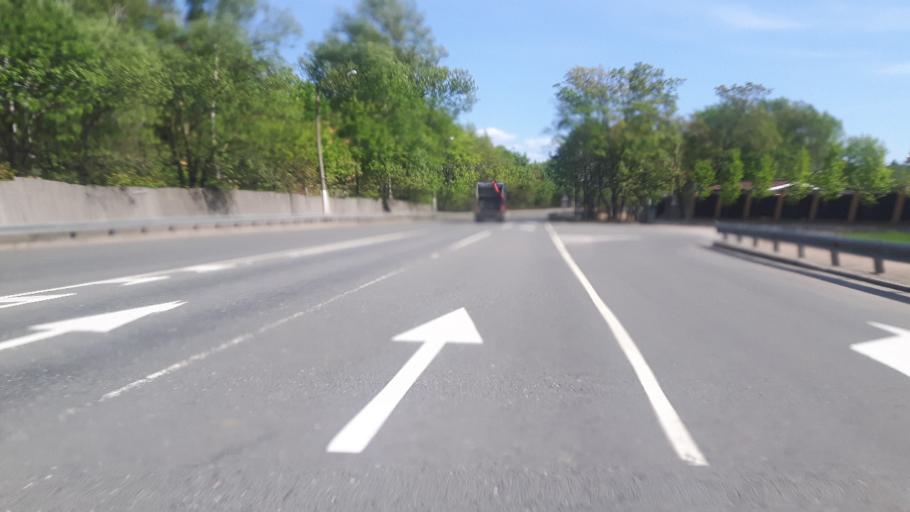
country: RU
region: Leningrad
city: Vyborg
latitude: 60.7277
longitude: 28.7041
